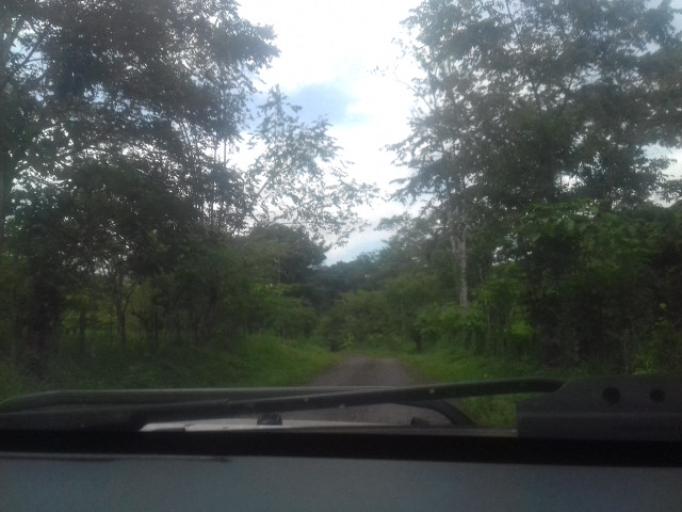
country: NI
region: Atlantico Norte (RAAN)
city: Waslala
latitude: 13.4965
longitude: -85.2315
